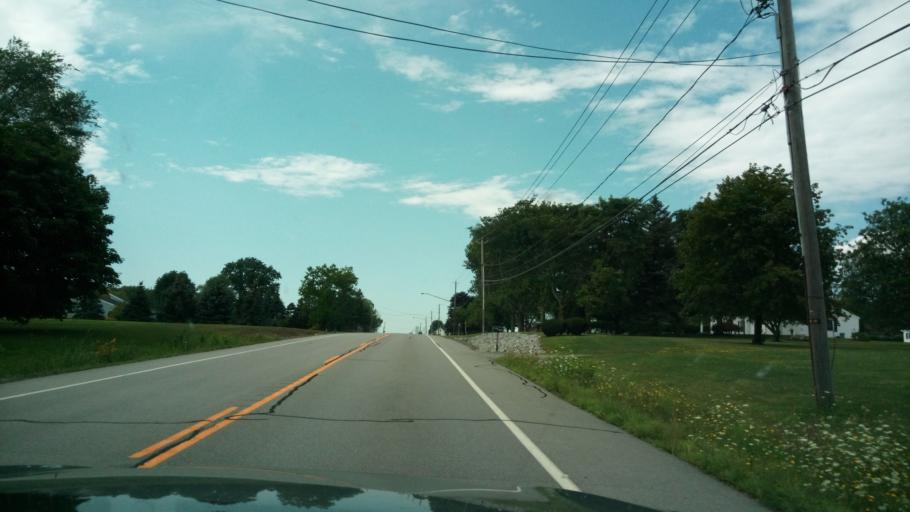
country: US
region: New York
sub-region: Livingston County
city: Geneseo
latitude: 42.8303
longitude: -77.8740
